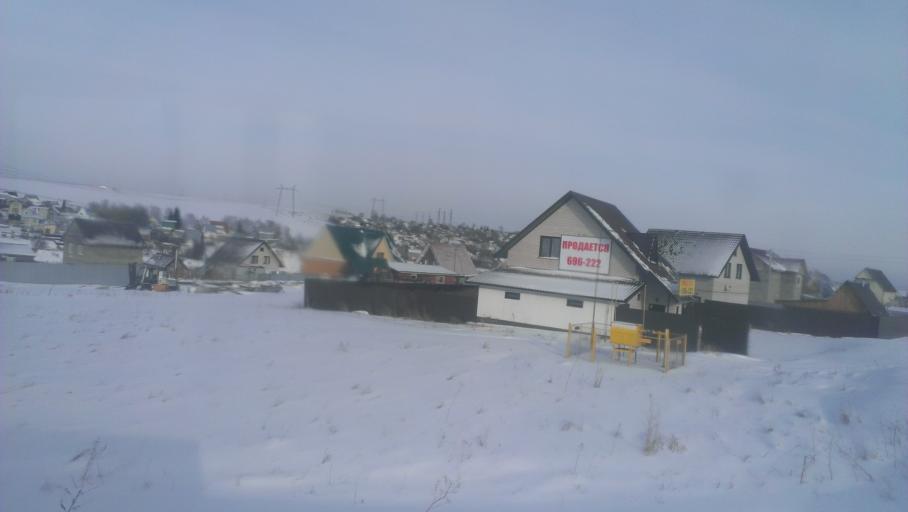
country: RU
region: Altai Krai
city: Gon'ba
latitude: 53.4136
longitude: 83.5530
